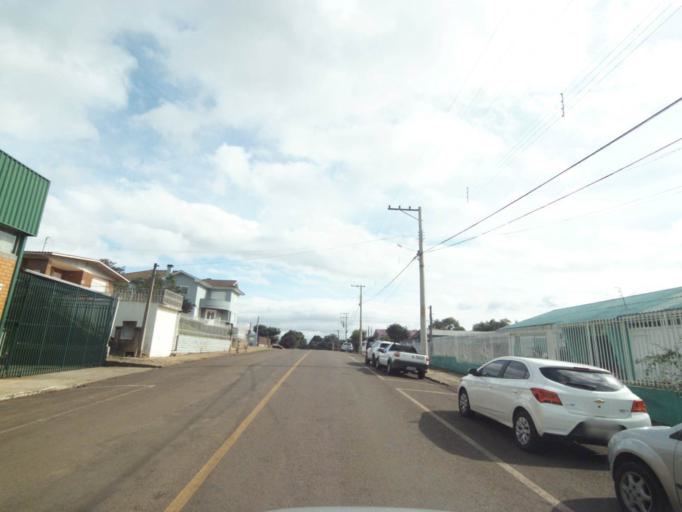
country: BR
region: Rio Grande do Sul
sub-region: Lagoa Vermelha
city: Lagoa Vermelha
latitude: -28.2099
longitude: -51.5326
